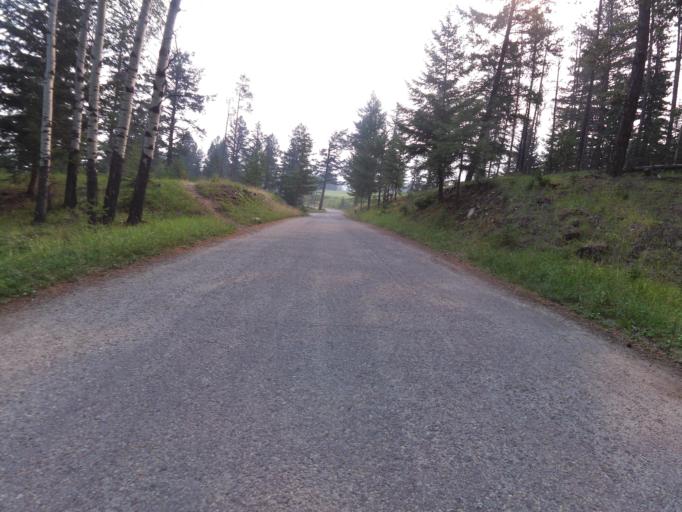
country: CA
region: Alberta
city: Jasper Park Lodge
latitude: 52.8794
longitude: -118.0568
